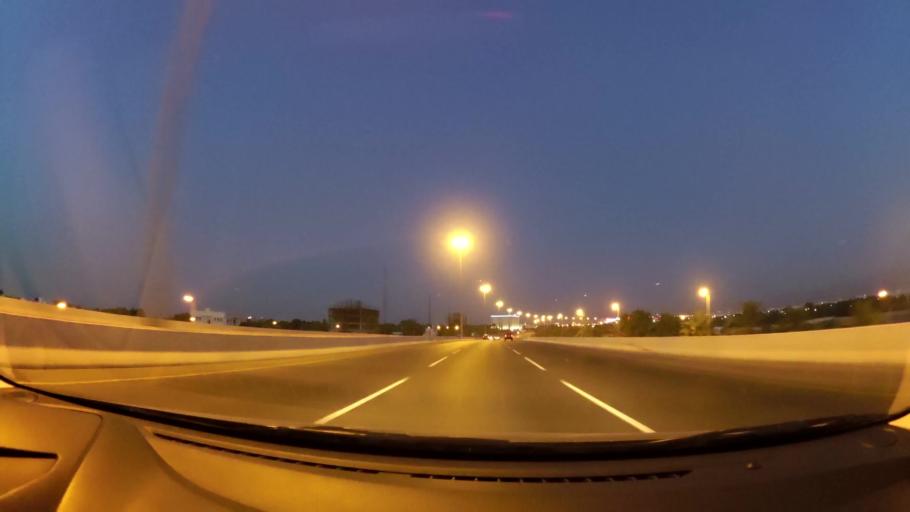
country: OM
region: Muhafazat Masqat
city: As Sib al Jadidah
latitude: 23.6540
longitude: 58.2074
